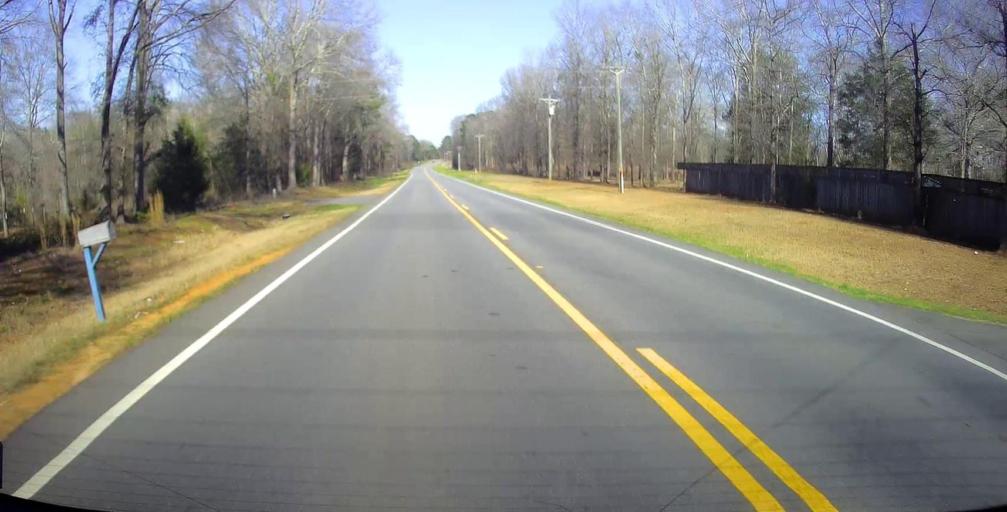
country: US
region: Georgia
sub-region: Macon County
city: Montezuma
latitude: 32.3146
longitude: -83.8974
